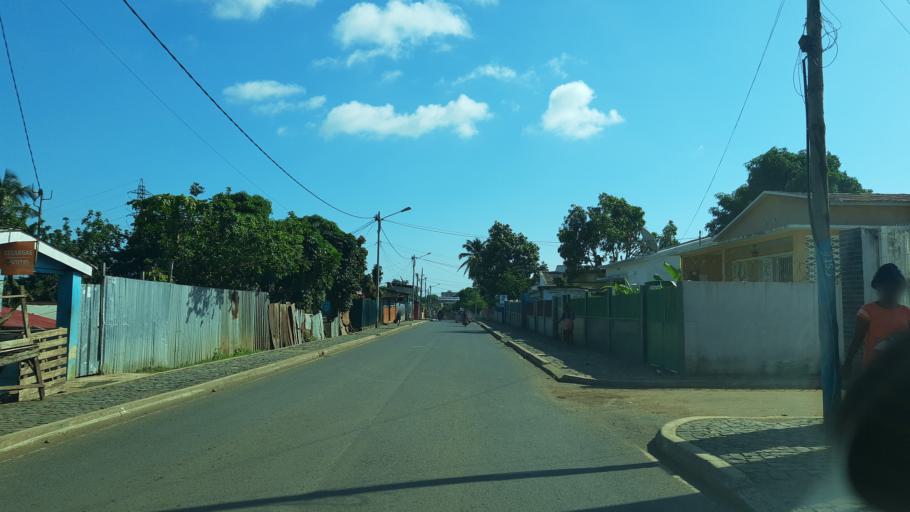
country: ST
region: Sao Tome Island
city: Sao Tome
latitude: 0.3310
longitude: 6.7303
